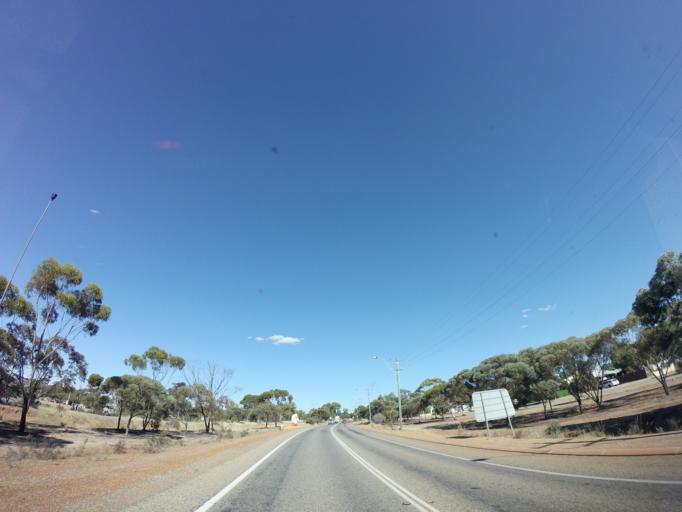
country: AU
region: Western Australia
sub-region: Merredin
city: Merredin
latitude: -31.4817
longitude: 118.2639
